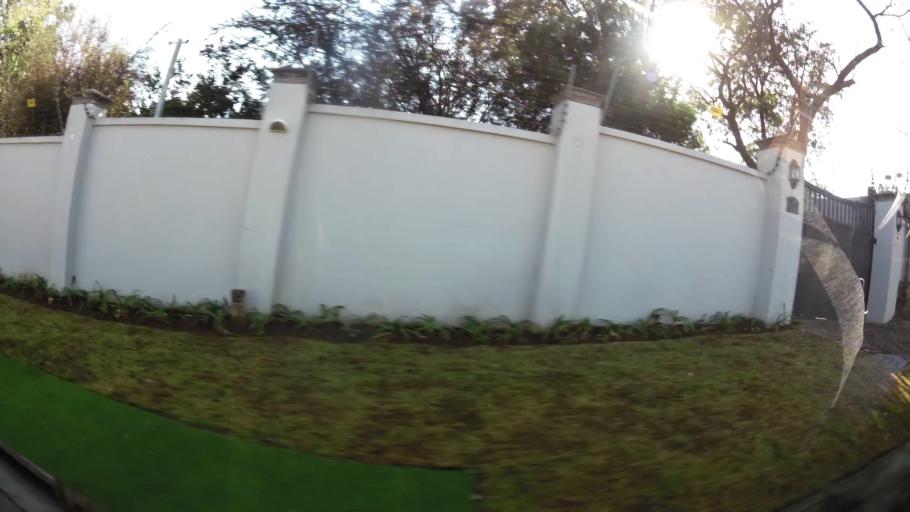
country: ZA
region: Gauteng
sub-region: City of Johannesburg Metropolitan Municipality
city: Midrand
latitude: -26.0718
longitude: 28.0389
